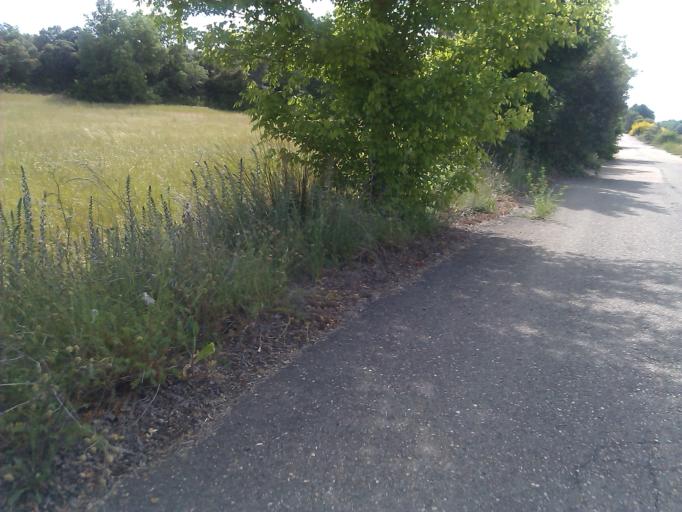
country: ES
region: Castille and Leon
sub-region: Provincia de Leon
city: San Justo de la Vega
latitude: 42.4477
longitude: -5.9686
